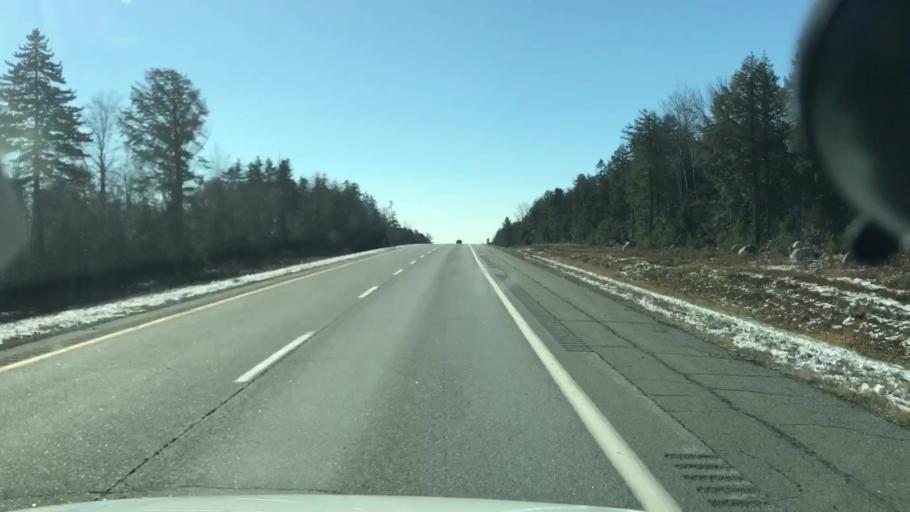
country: US
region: Maine
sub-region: Penobscot County
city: Howland
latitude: 45.2835
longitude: -68.6697
